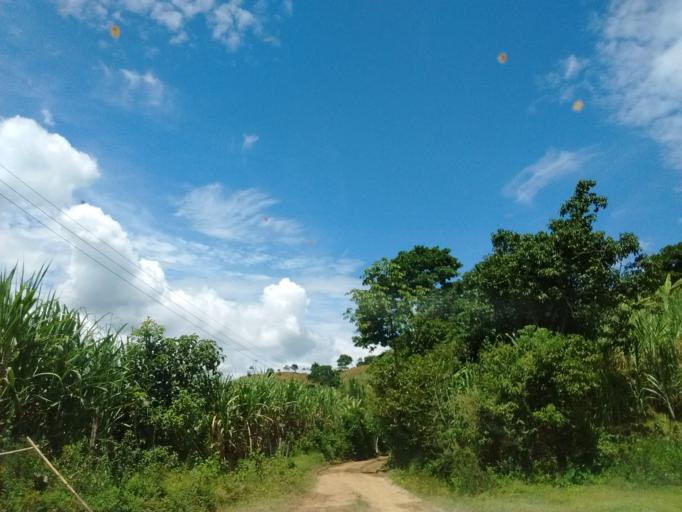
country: CO
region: Cauca
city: Villa Rica
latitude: 2.6592
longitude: -76.7677
